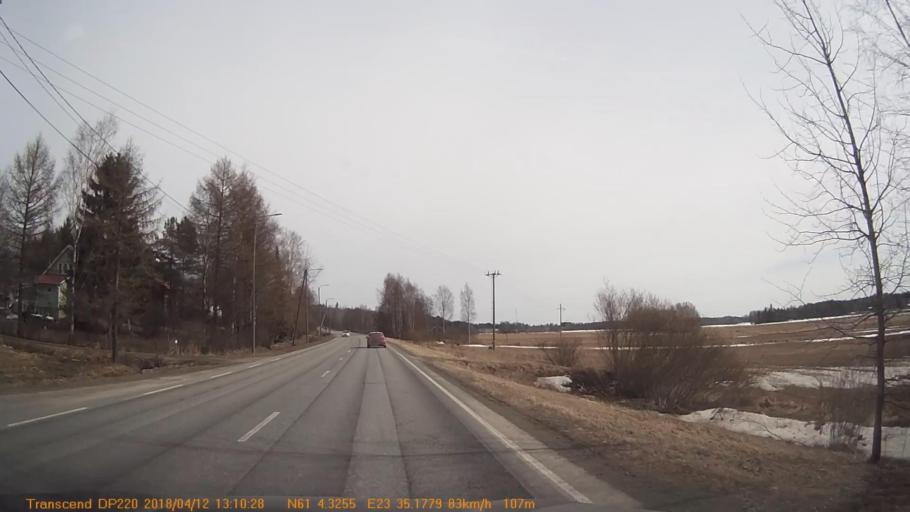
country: FI
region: Pirkanmaa
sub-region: Etelae-Pirkanmaa
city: Urjala
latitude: 61.0719
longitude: 23.5880
